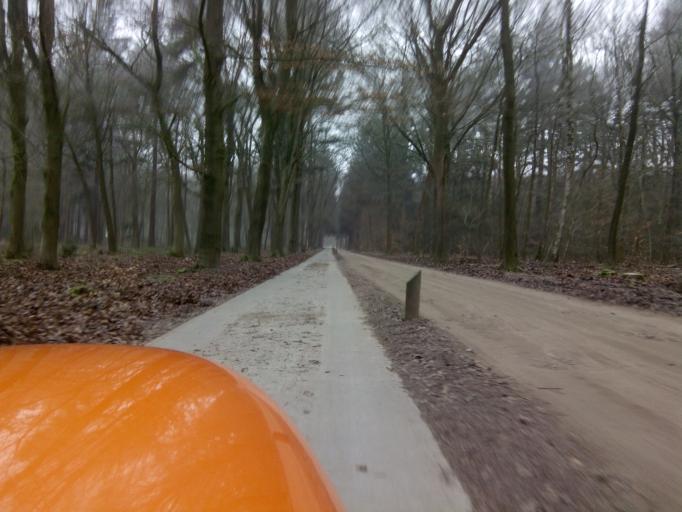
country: NL
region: Gelderland
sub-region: Gemeente Putten
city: Putten
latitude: 52.2404
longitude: 5.6475
